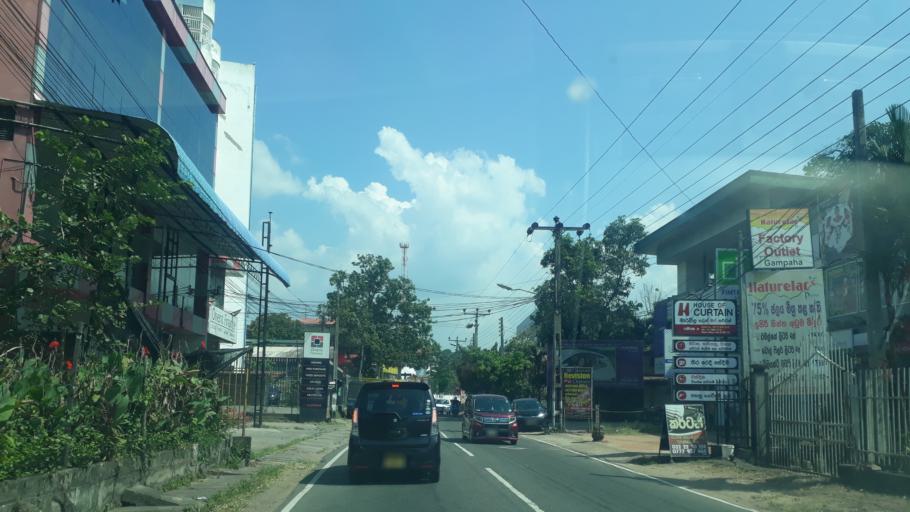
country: LK
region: Western
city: Gampaha
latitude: 7.0887
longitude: 80.0057
